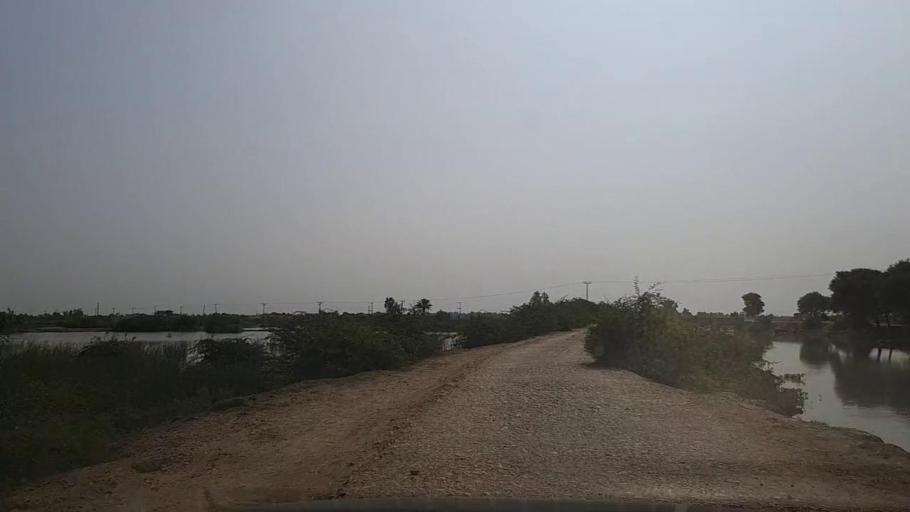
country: PK
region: Sindh
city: Chuhar Jamali
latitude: 24.5420
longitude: 67.9125
